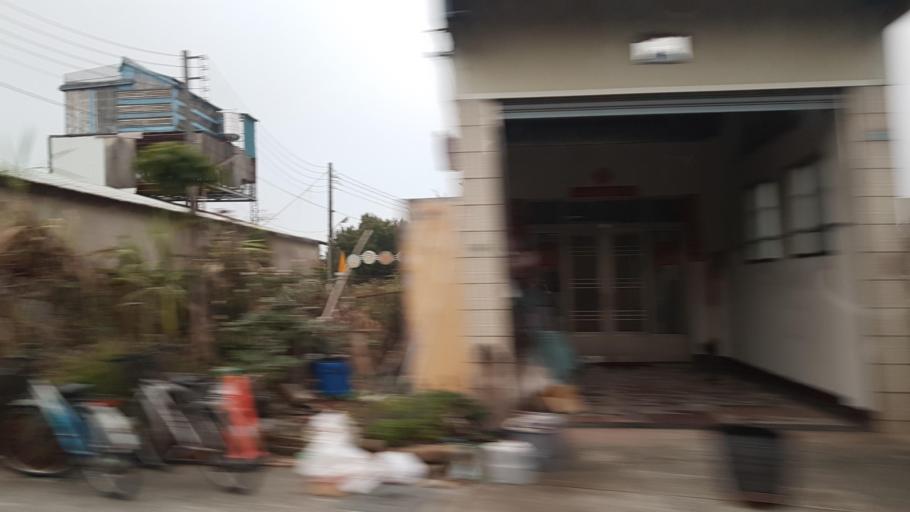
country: TW
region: Taiwan
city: Xinying
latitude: 23.3578
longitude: 120.4213
